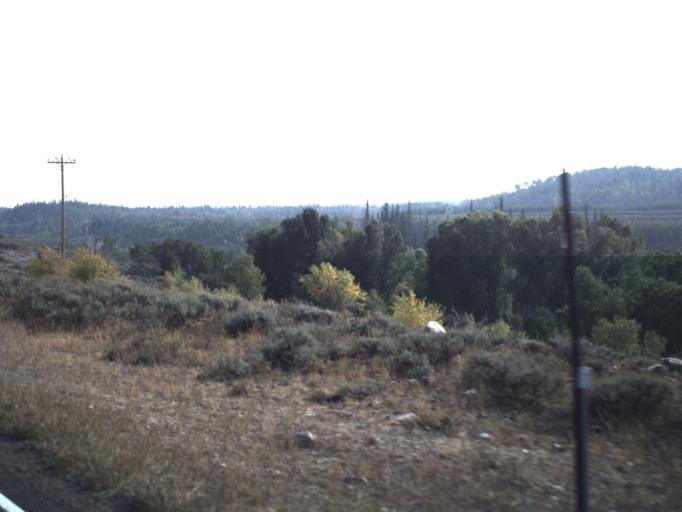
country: US
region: Wyoming
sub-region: Uinta County
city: Evanston
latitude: 40.9512
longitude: -110.8412
